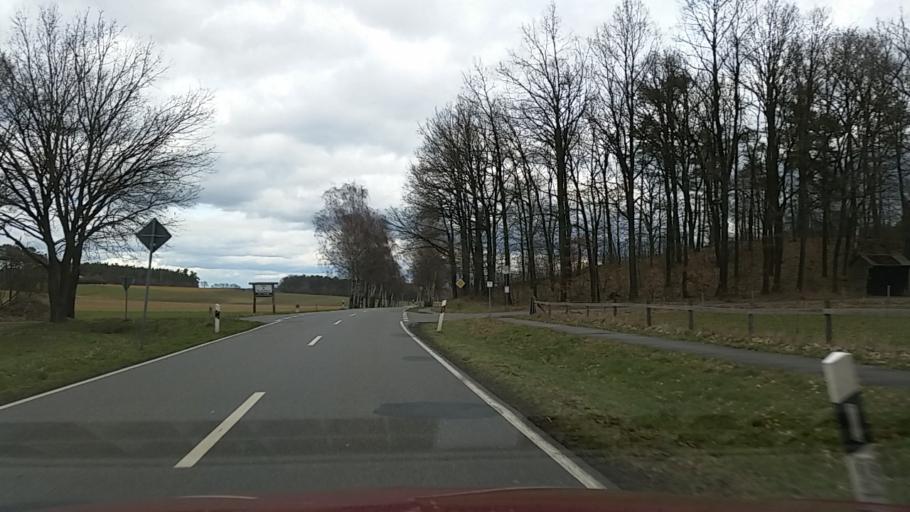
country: DE
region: Lower Saxony
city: Gohrde
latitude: 53.1138
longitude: 10.9483
